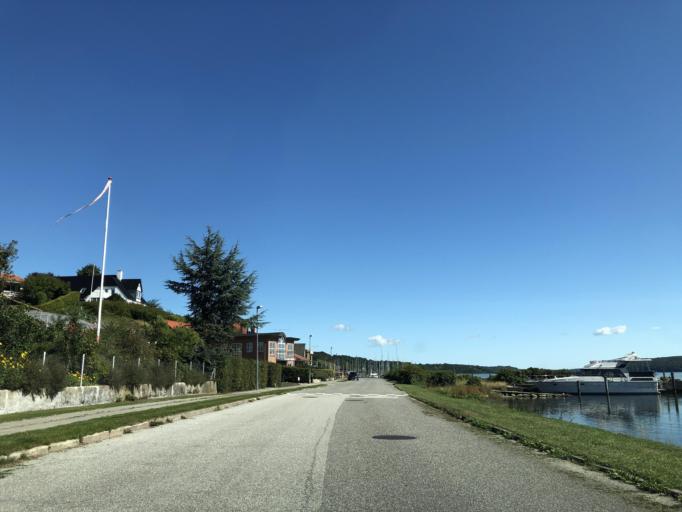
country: DK
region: North Denmark
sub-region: Mariagerfjord Kommune
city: Hobro
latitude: 56.6416
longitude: 9.8056
